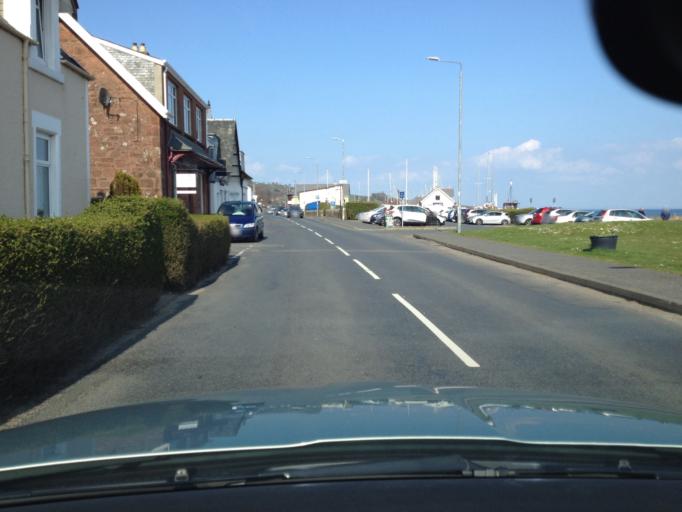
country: GB
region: Scotland
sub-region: North Ayrshire
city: Lamlash
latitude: 55.5344
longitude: -5.1266
